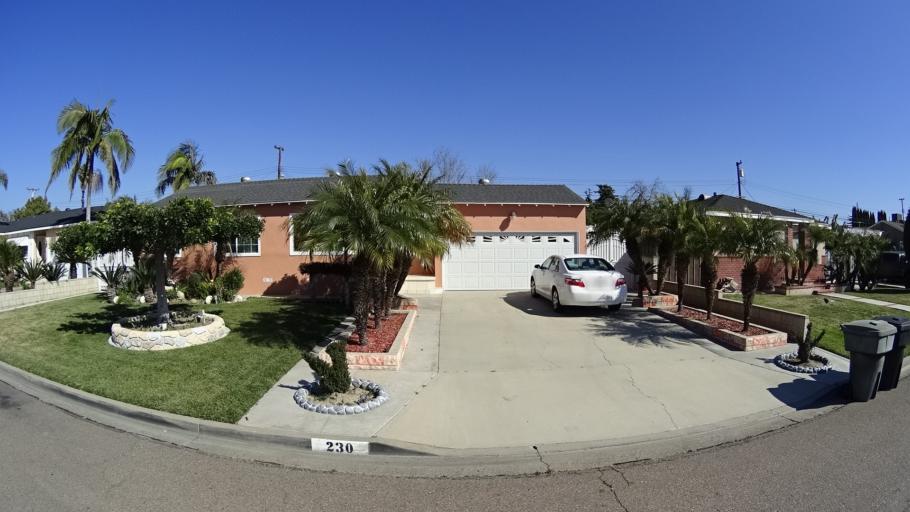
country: US
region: California
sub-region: Orange County
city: Anaheim
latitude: 33.8350
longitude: -117.9543
